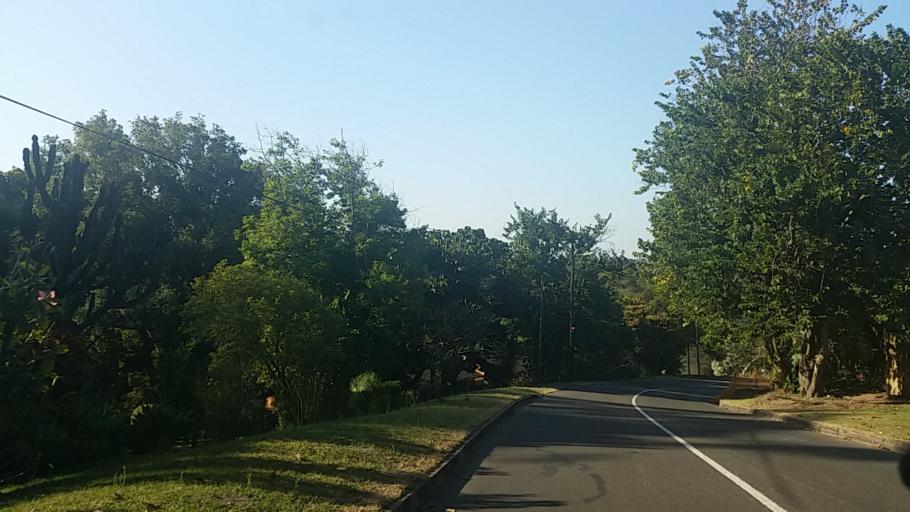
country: ZA
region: KwaZulu-Natal
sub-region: eThekwini Metropolitan Municipality
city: Berea
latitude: -29.8490
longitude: 30.9117
